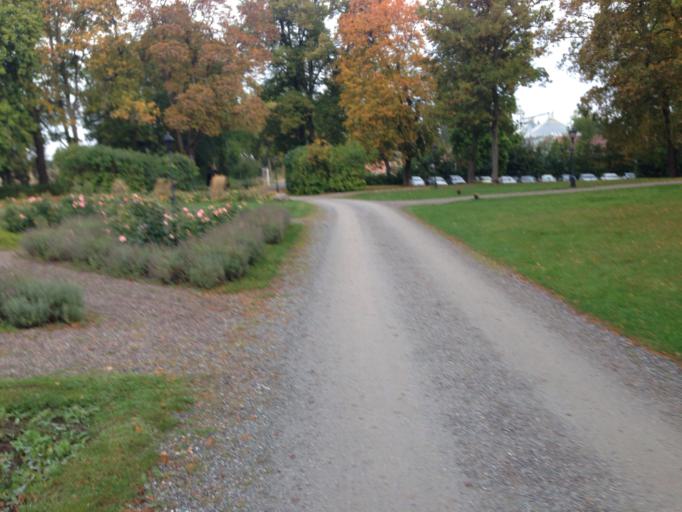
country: SE
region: Uppsala
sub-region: Enkopings Kommun
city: Enkoping
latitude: 59.6048
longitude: 17.0493
